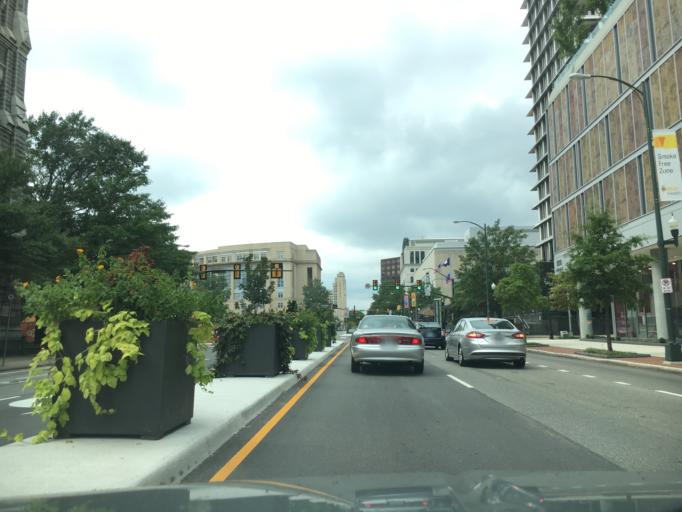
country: US
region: Virginia
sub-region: City of Richmond
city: Richmond
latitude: 37.5399
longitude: -77.4324
